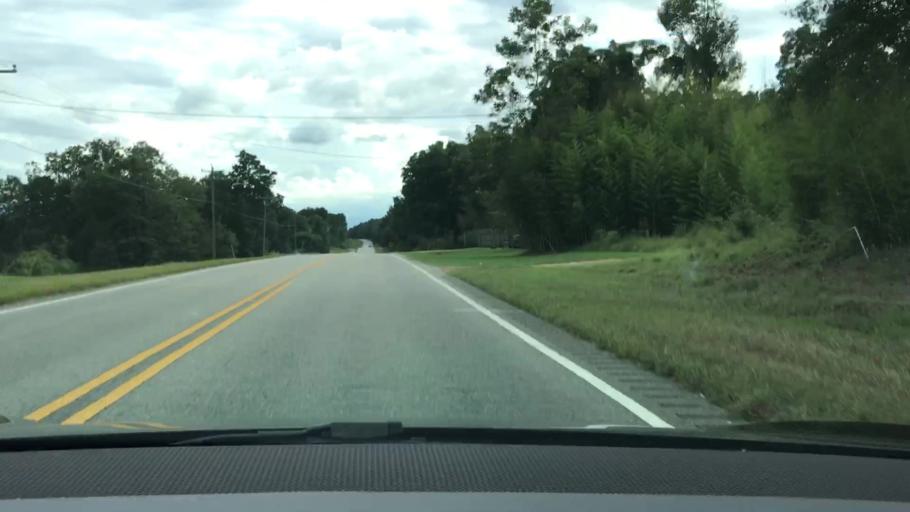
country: US
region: Alabama
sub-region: Pike County
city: Troy
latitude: 31.6488
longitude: -85.9694
